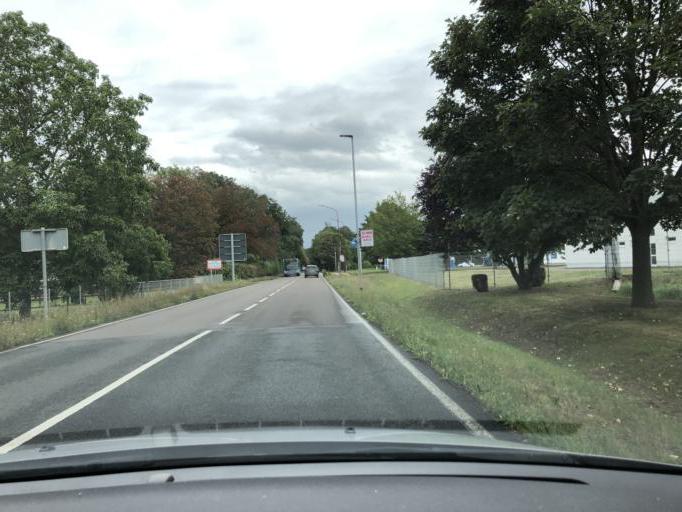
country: DE
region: Saxony-Anhalt
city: Koethen
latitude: 51.7555
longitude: 11.9468
